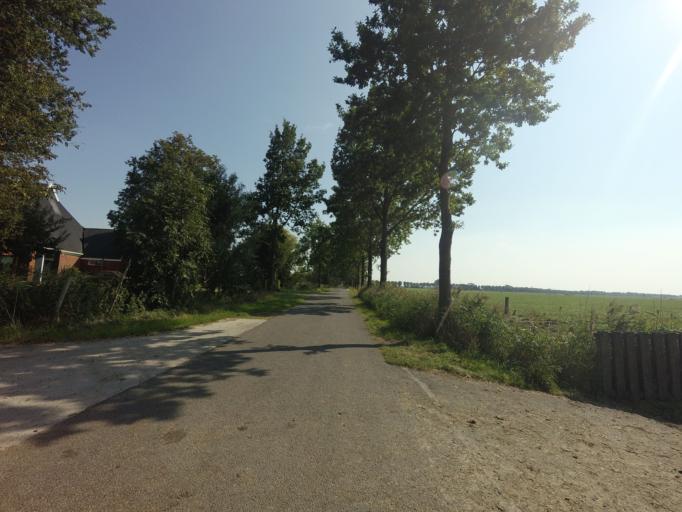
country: NL
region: Groningen
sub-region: Gemeente Zuidhorn
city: Zuidhorn
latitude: 53.2332
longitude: 6.4226
